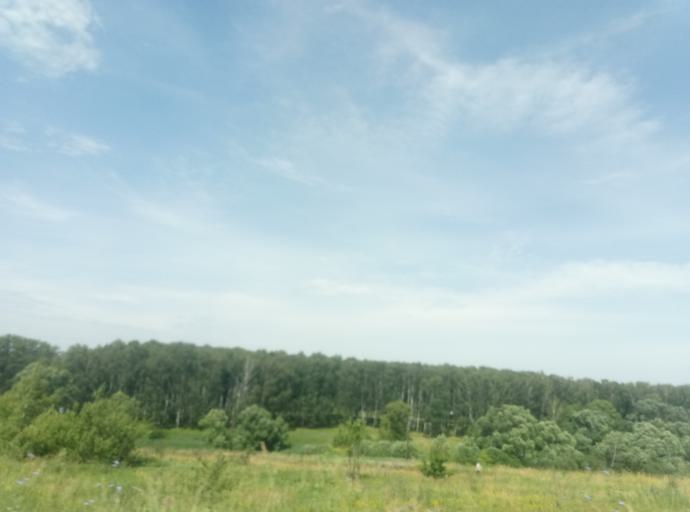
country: RU
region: Tula
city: Kireyevsk
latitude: 53.9260
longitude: 37.9468
